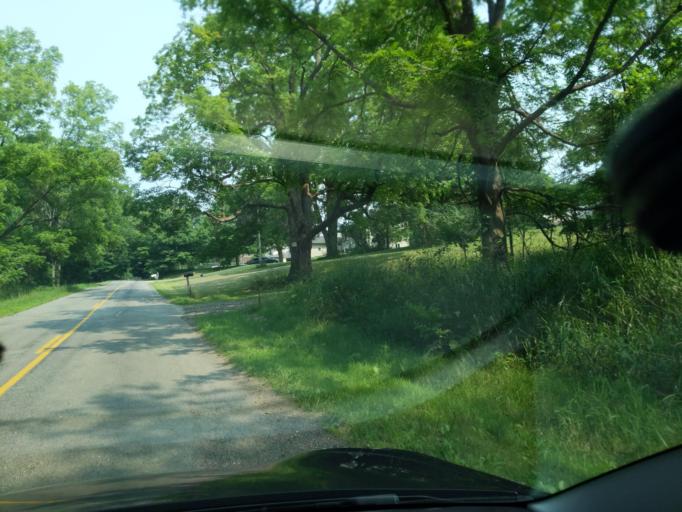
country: US
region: Michigan
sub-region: Ingham County
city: Holt
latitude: 42.6113
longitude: -84.5702
